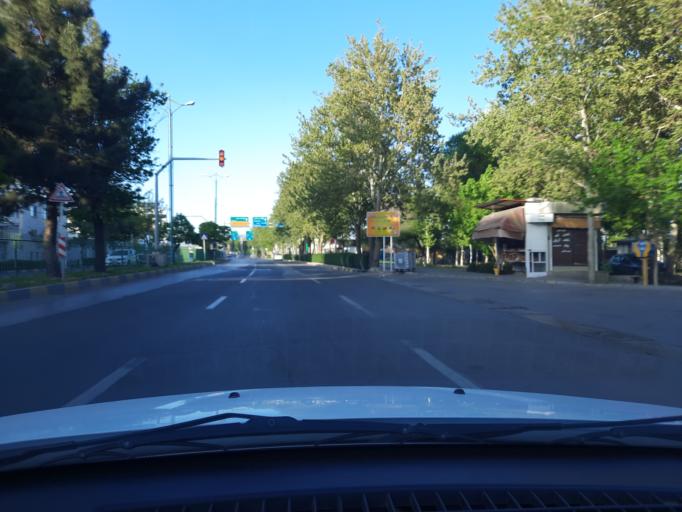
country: IR
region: Qazvin
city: Qazvin
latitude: 36.2701
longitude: 50.0216
